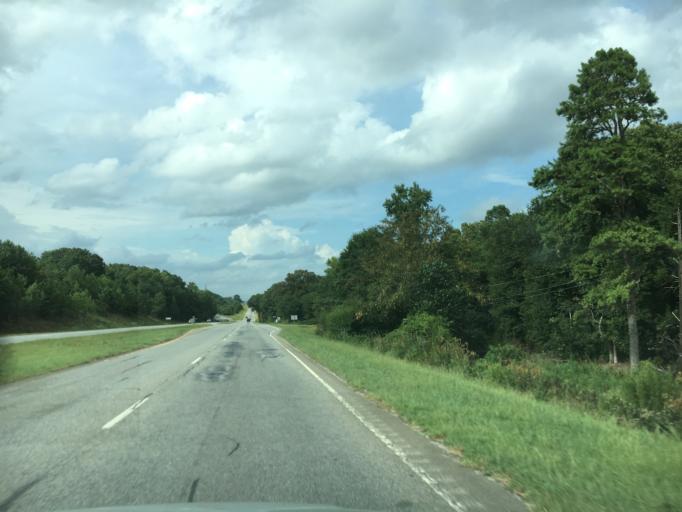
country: US
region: South Carolina
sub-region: Anderson County
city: Piedmont
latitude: 34.6839
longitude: -82.5064
